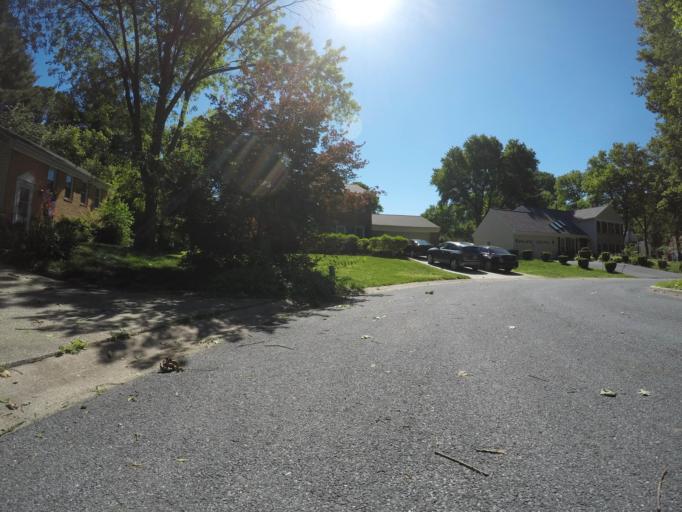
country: US
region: Maryland
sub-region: Howard County
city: Columbia
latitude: 39.2372
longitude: -76.8606
